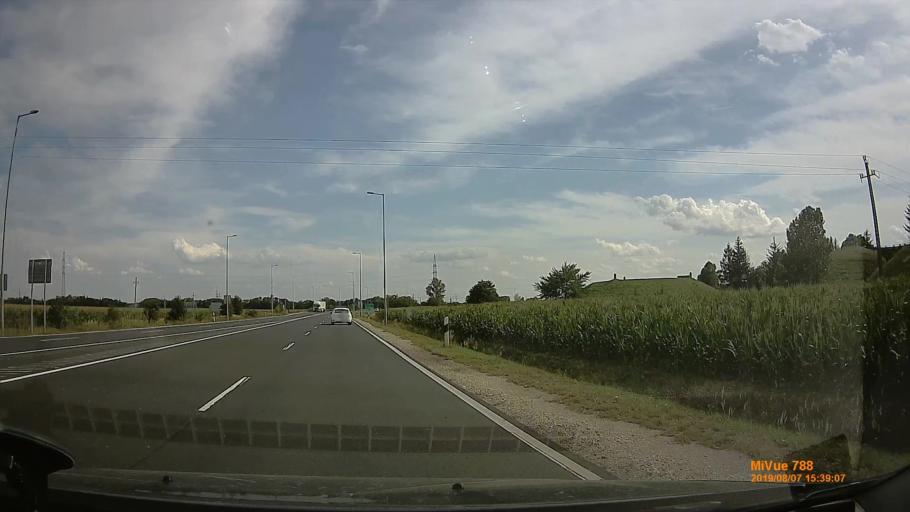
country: HU
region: Vas
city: Szombathely
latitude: 47.2257
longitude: 16.6571
